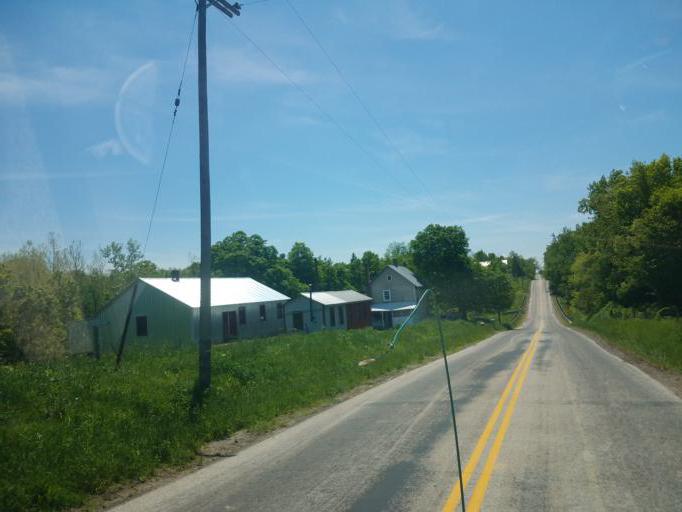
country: US
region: Ohio
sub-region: Ashland County
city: Ashland
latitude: 40.9619
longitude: -82.2438
